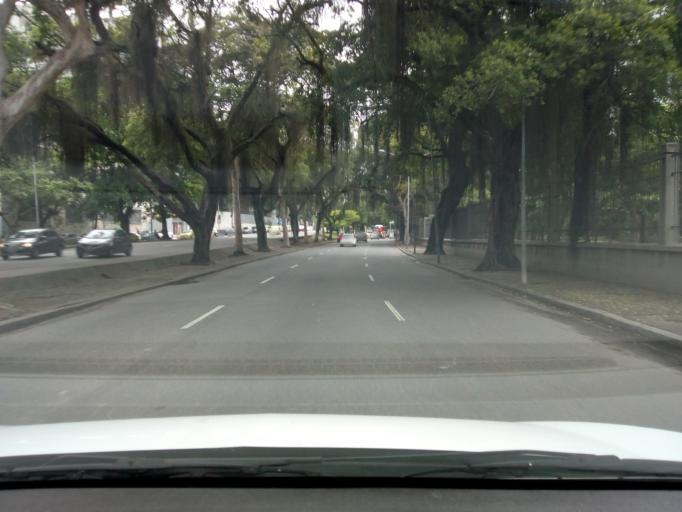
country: BR
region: Rio de Janeiro
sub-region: Rio De Janeiro
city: Rio de Janeiro
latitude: -22.9060
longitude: -43.2207
